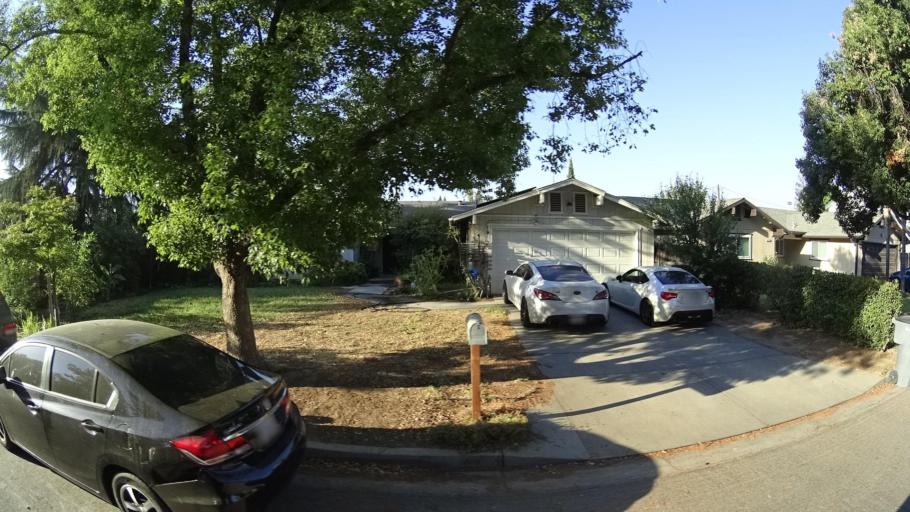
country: US
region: California
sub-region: Fresno County
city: Sunnyside
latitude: 36.7371
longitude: -119.7085
